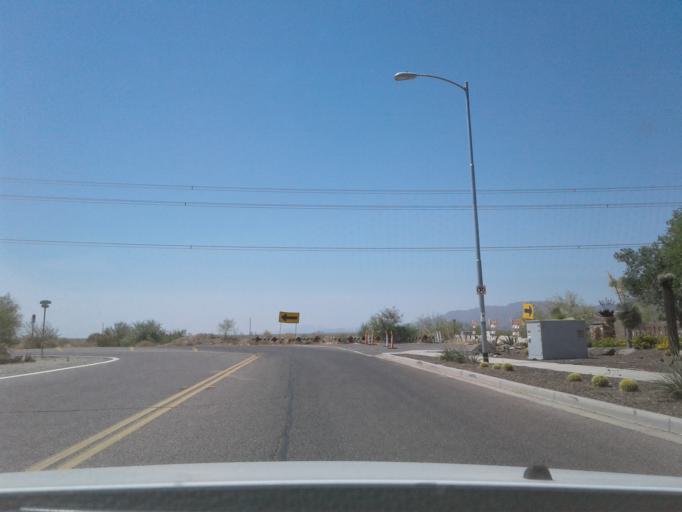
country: US
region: Arizona
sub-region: Maricopa County
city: Laveen
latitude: 33.2916
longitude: -112.1173
